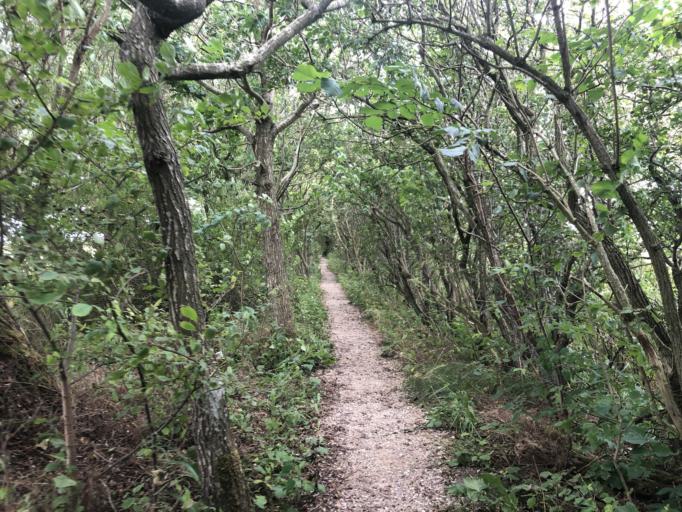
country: DK
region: Central Jutland
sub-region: Ringkobing-Skjern Kommune
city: Skjern
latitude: 55.9032
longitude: 8.4228
